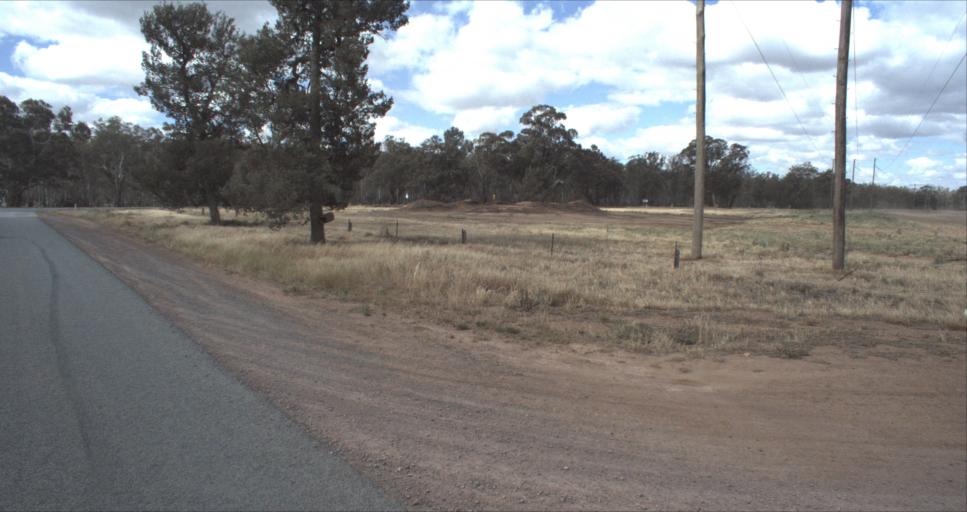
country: AU
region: New South Wales
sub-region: Leeton
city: Leeton
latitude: -34.6442
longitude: 146.3525
